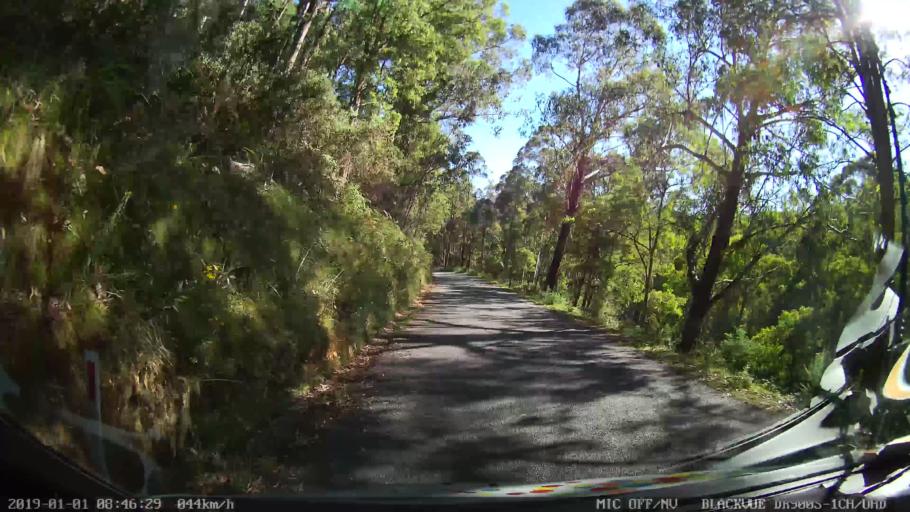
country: AU
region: New South Wales
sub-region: Snowy River
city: Jindabyne
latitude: -36.3000
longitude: 148.1937
